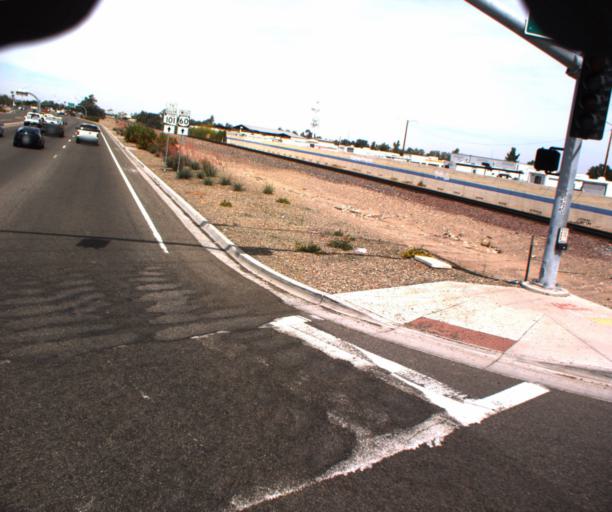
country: US
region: Arizona
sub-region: Maricopa County
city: Sun City
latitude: 33.5927
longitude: -112.2553
